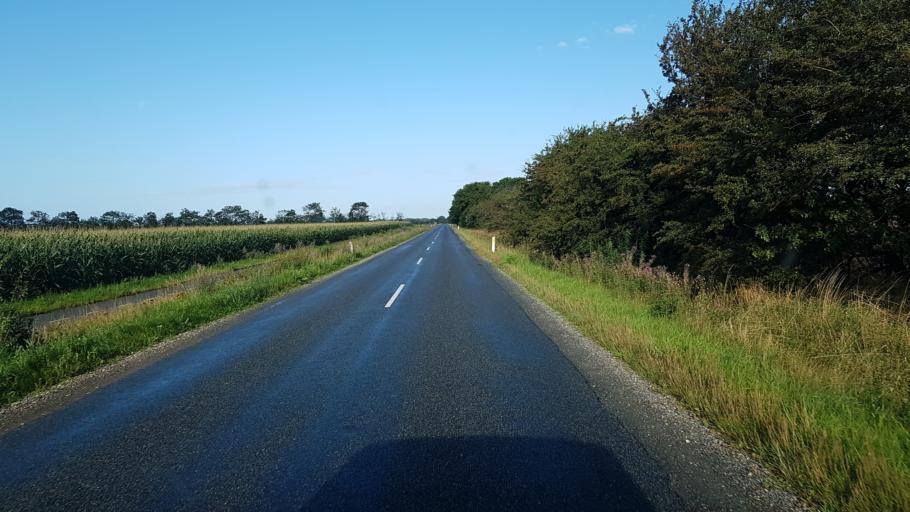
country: DK
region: South Denmark
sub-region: Esbjerg Kommune
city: Bramming
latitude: 55.4837
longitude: 8.7307
